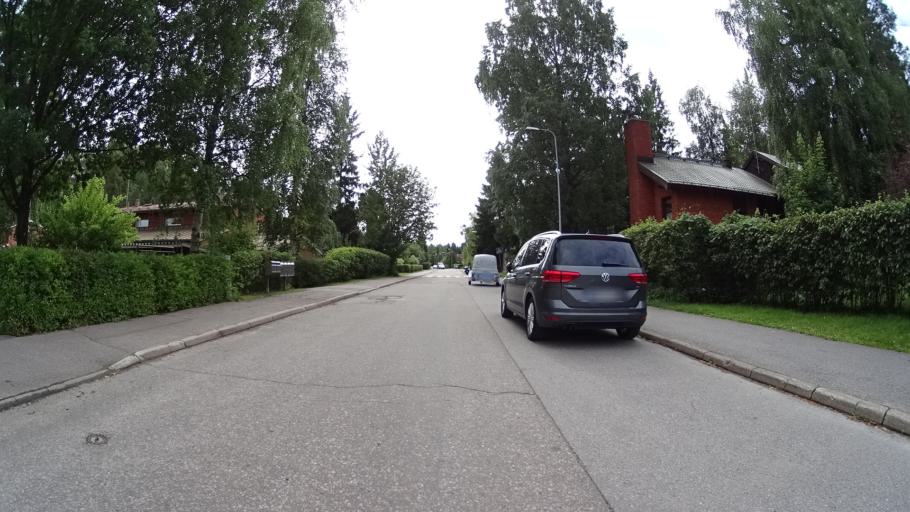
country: FI
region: Uusimaa
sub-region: Helsinki
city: Helsinki
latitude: 60.2518
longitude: 24.9290
